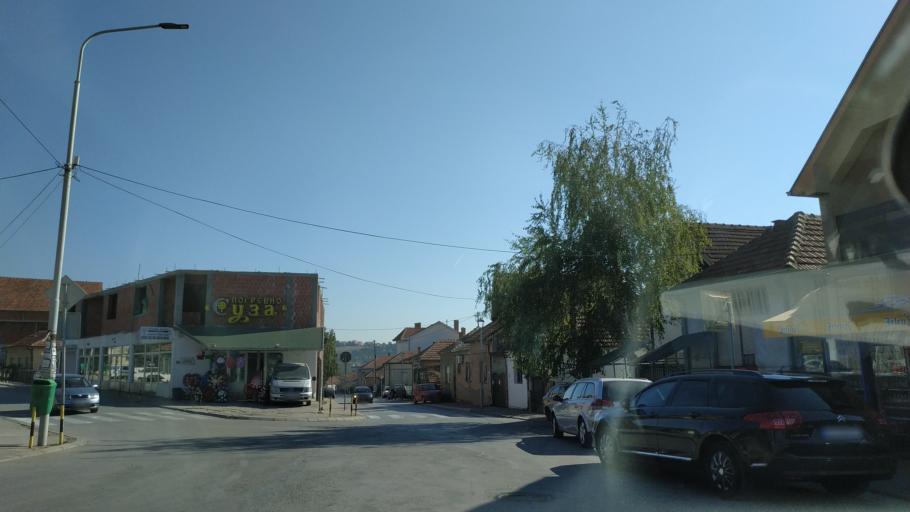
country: RS
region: Central Serbia
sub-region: Nisavski Okrug
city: Aleksinac
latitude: 43.5393
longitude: 21.7009
